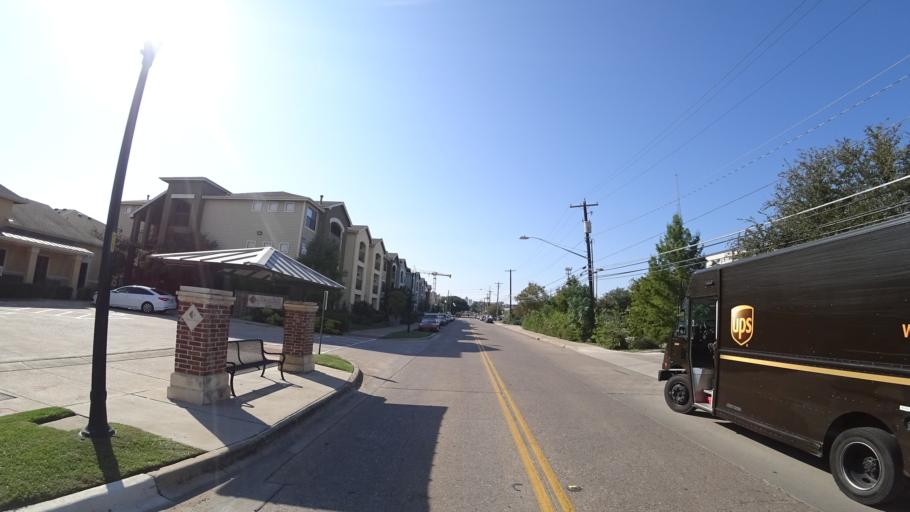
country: US
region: Texas
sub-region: Travis County
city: Austin
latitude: 30.2607
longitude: -97.7199
